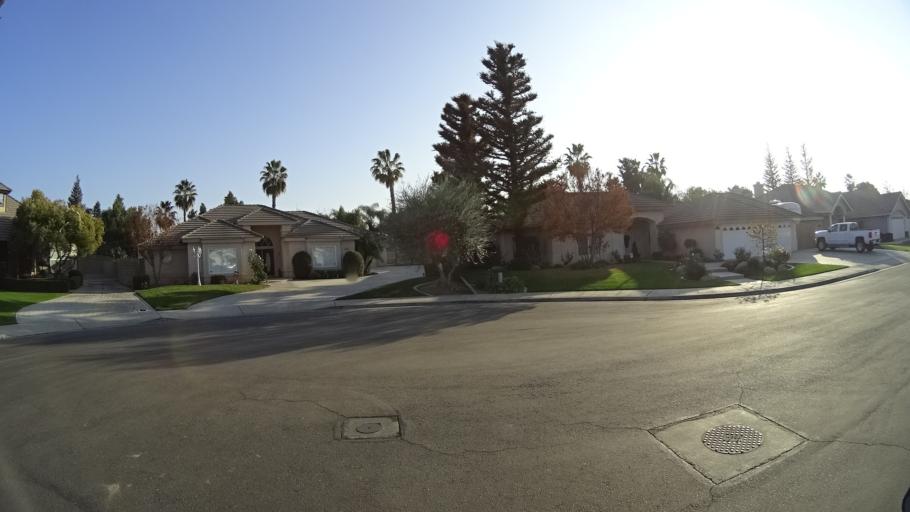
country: US
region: California
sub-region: Kern County
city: Rosedale
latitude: 35.3769
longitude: -119.1493
